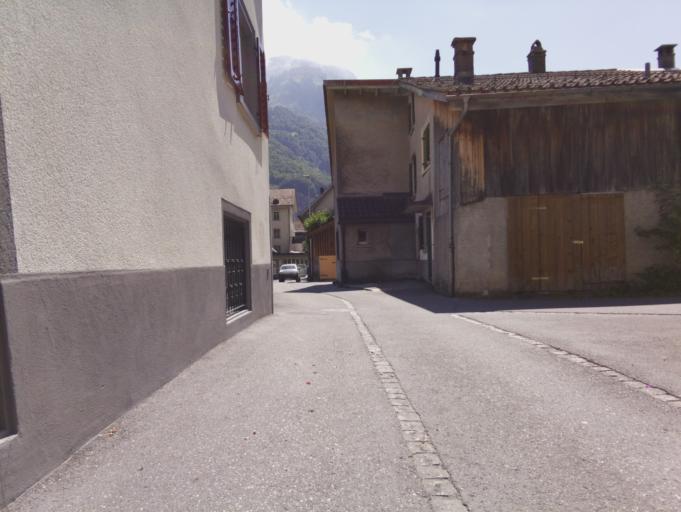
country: CH
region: Glarus
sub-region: Glarus
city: Netstal
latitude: 47.0596
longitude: 9.0513
